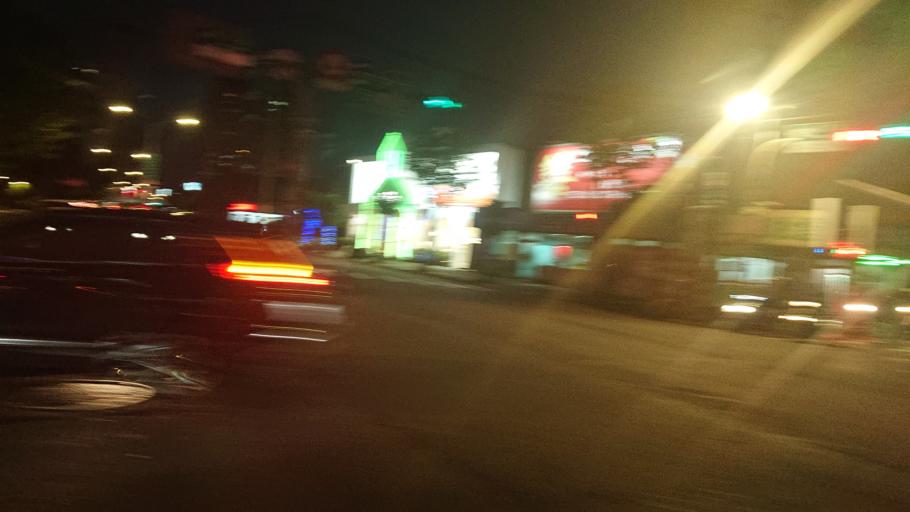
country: TW
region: Taiwan
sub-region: Taoyuan
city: Taoyuan
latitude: 24.9390
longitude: 121.3685
